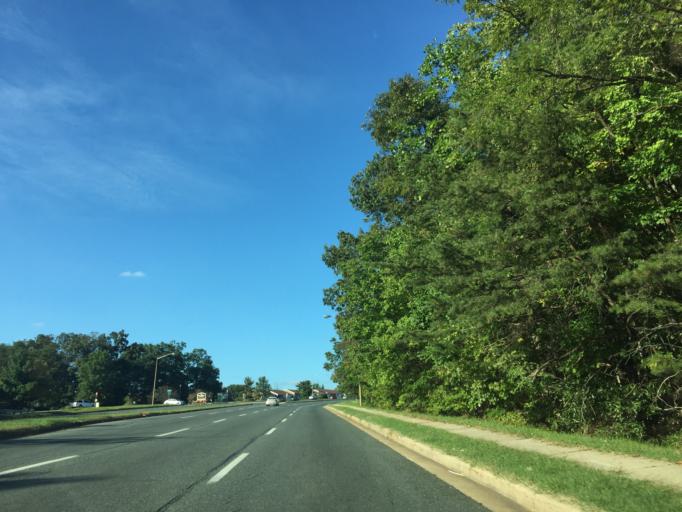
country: US
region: Maryland
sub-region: Baltimore County
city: Rossville
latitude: 39.3429
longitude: -76.4872
